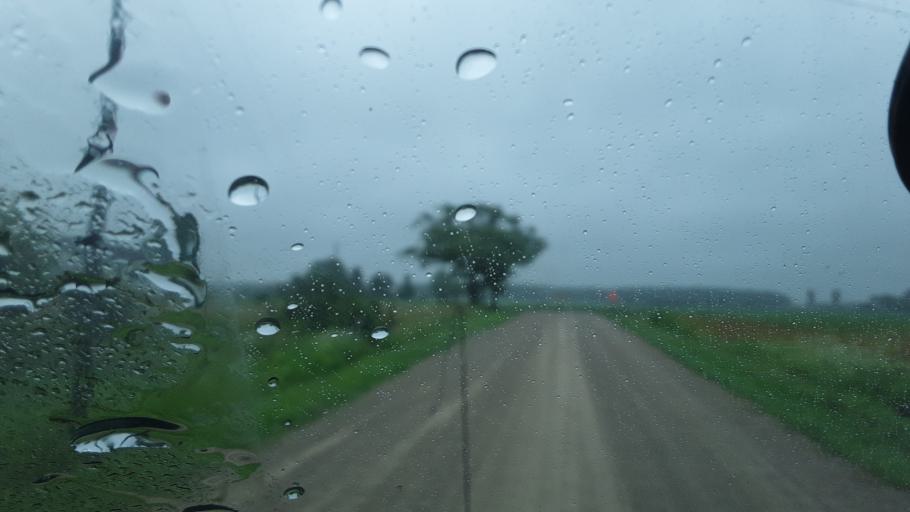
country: US
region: Indiana
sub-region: Adams County
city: Berne
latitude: 40.6351
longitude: -84.9940
